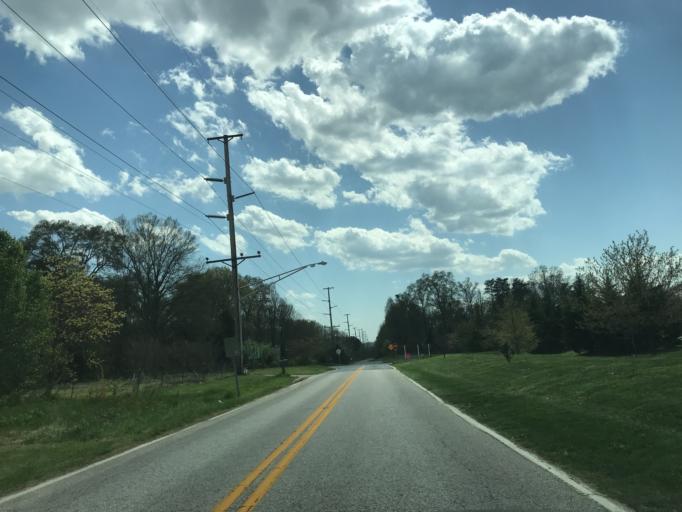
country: US
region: Maryland
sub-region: Anne Arundel County
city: Odenton
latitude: 39.1053
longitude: -76.6885
